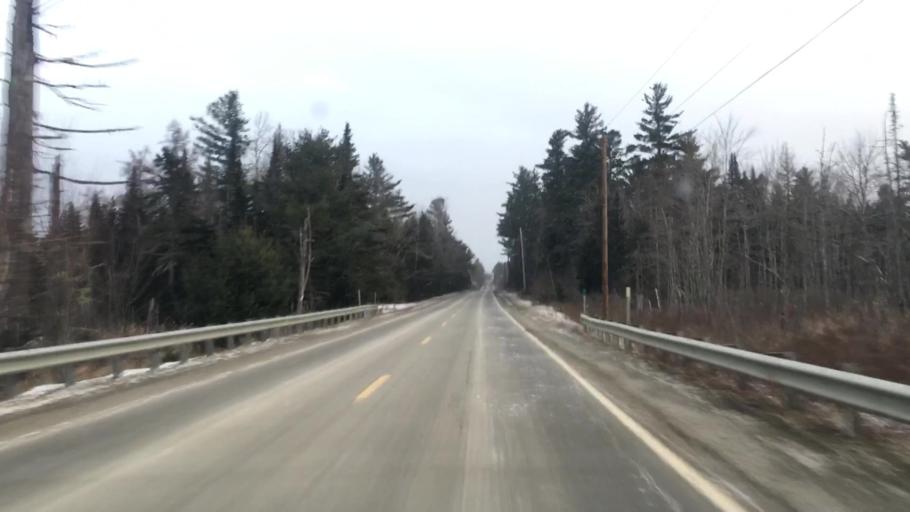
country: US
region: Maine
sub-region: Hancock County
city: Ellsworth
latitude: 44.6721
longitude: -68.3541
